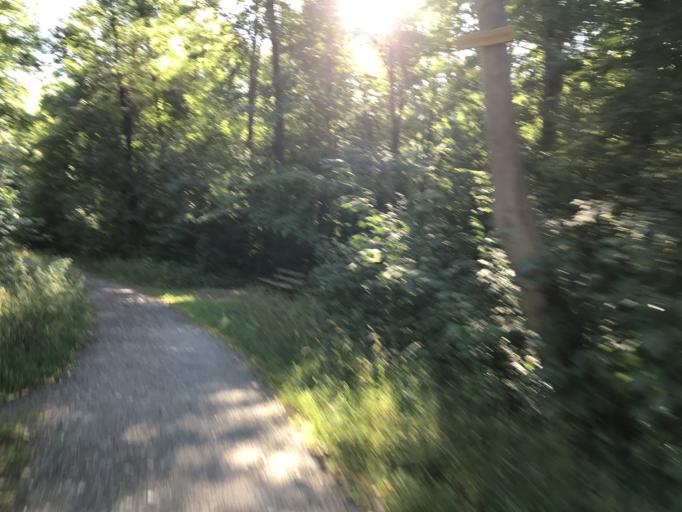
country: DE
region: Baden-Wuerttemberg
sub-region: Regierungsbezirk Stuttgart
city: Leinfelden-Echterdingen
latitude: 48.7413
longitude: 9.1397
